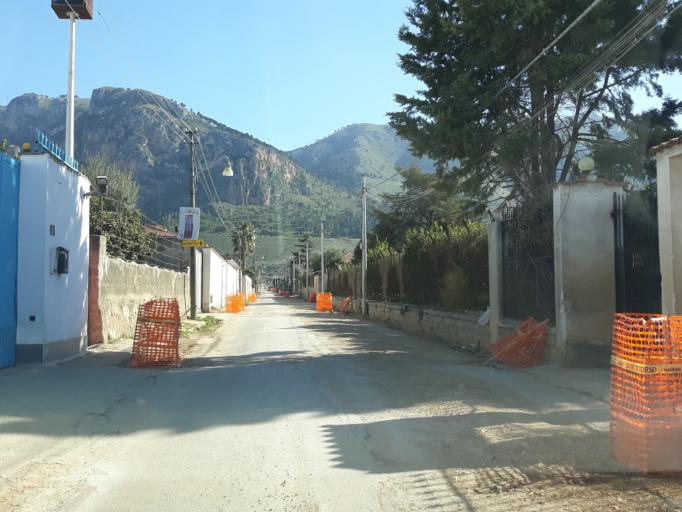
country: IT
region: Sicily
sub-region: Palermo
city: Villa Ciambra
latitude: 38.0829
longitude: 13.3459
